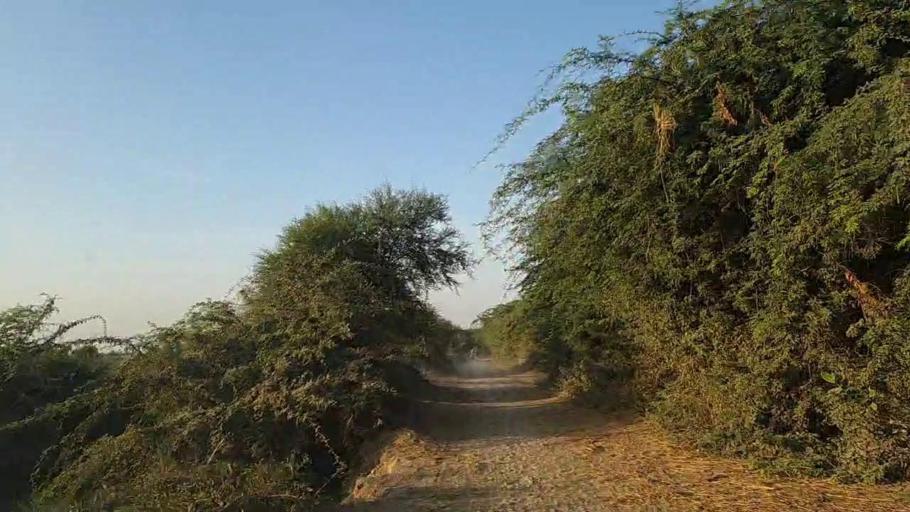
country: PK
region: Sindh
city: Mirpur Batoro
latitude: 24.7154
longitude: 68.2147
